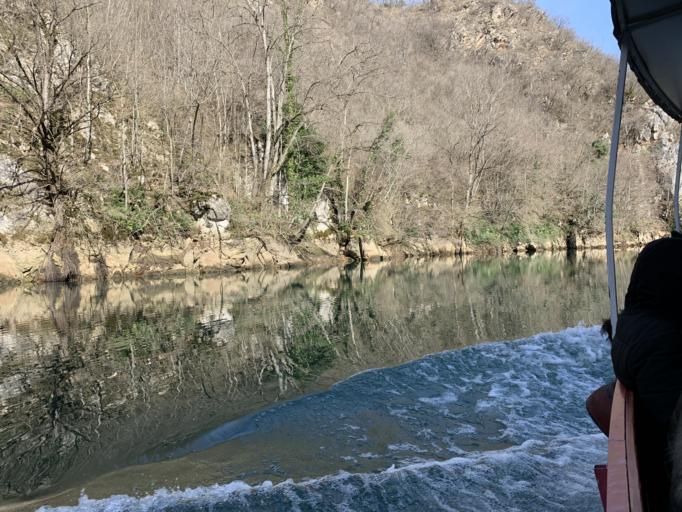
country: MK
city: Grchec
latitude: 41.9313
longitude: 21.2936
